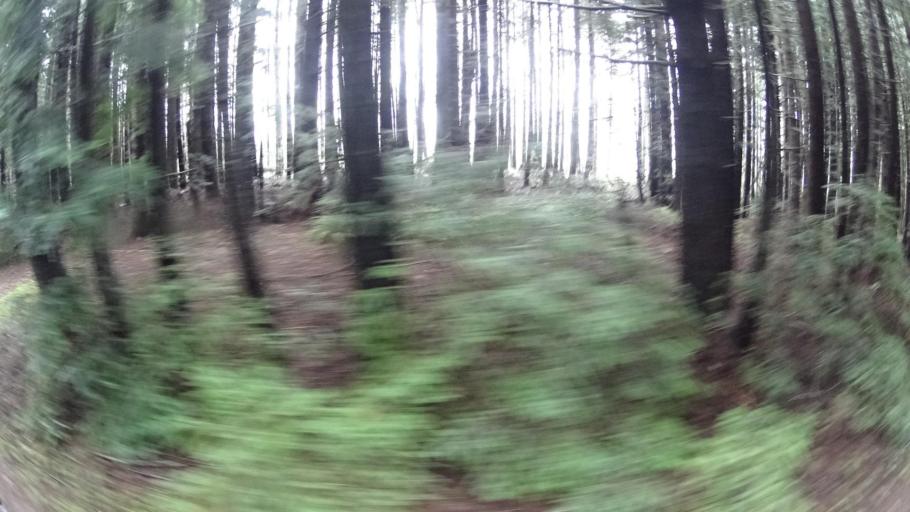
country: US
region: California
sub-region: Humboldt County
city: Westhaven-Moonstone
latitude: 41.2324
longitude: -123.9783
